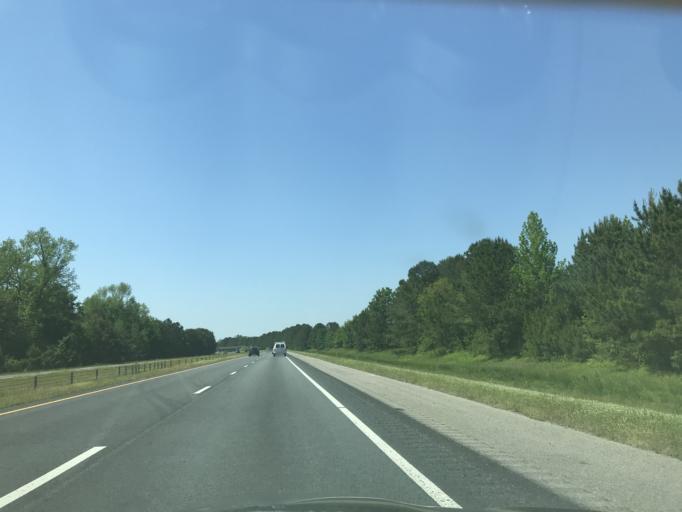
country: US
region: North Carolina
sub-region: Johnston County
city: Benson
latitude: 35.3351
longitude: -78.4601
